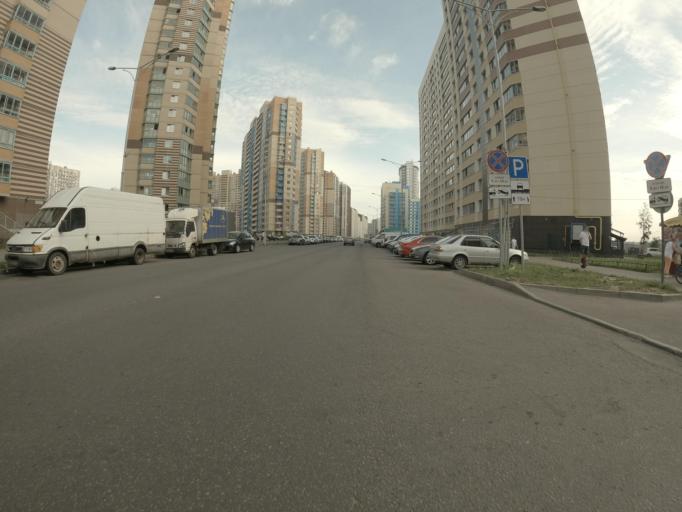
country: RU
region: Leningrad
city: Rybatskoye
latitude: 59.9062
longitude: 30.5127
